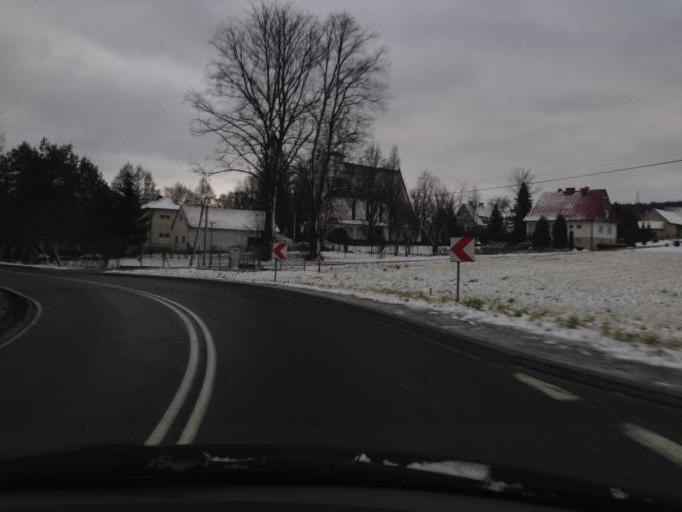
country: PL
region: Lesser Poland Voivodeship
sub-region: Powiat tarnowski
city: Rzepiennik Strzyzewski
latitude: 49.8232
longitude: 21.0079
